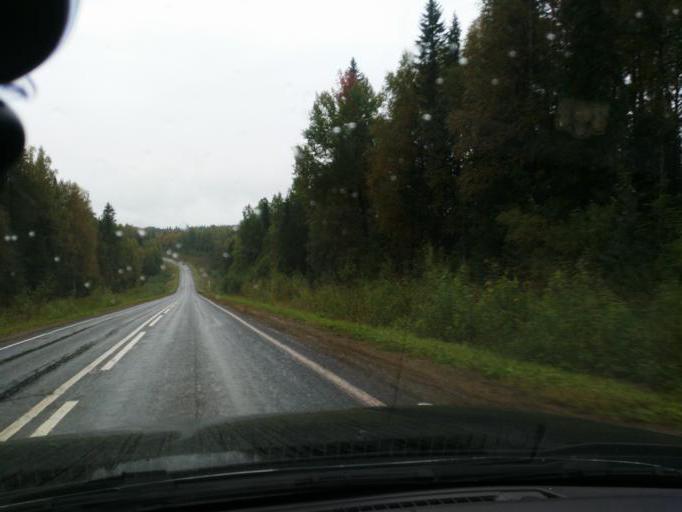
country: RU
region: Perm
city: Yugo-Kamskiy
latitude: 57.5903
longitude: 55.6675
